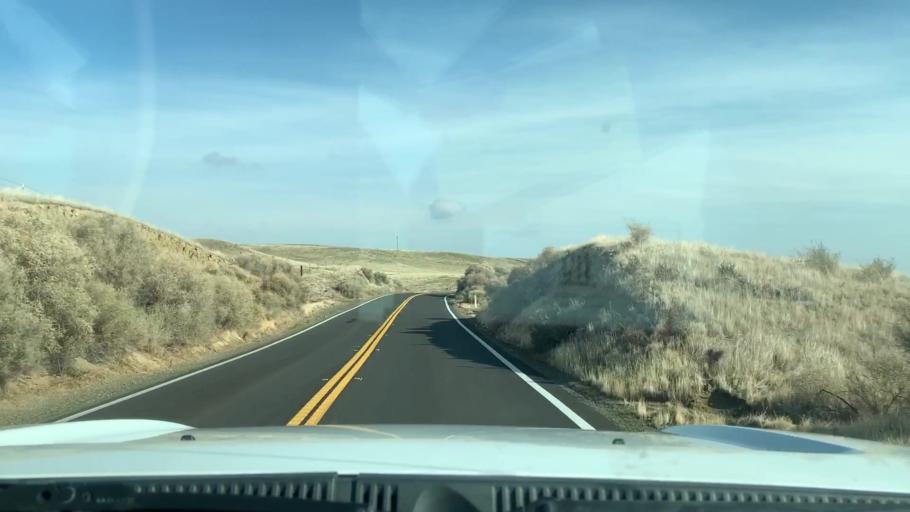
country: US
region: California
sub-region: Fresno County
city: Coalinga
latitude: 36.1143
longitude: -120.3833
